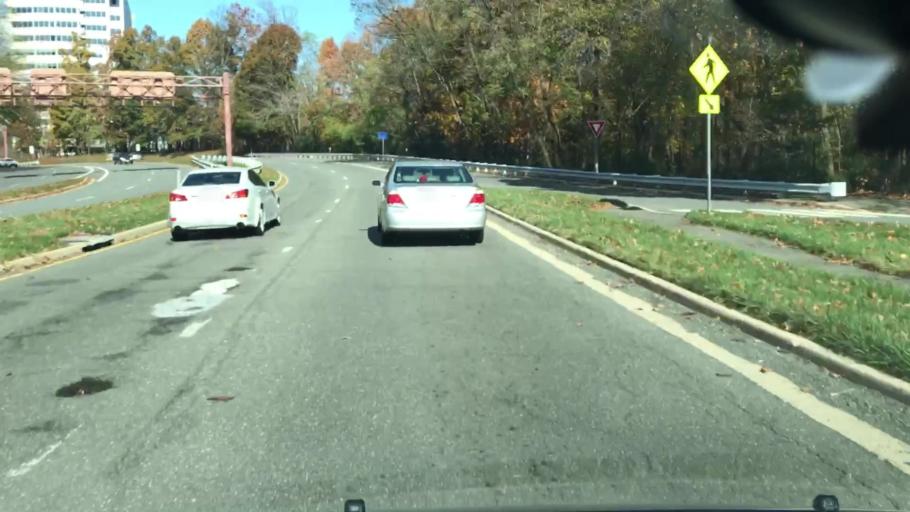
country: US
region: Virginia
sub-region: Fairfax County
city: Merrifield
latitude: 38.8665
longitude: -77.2138
